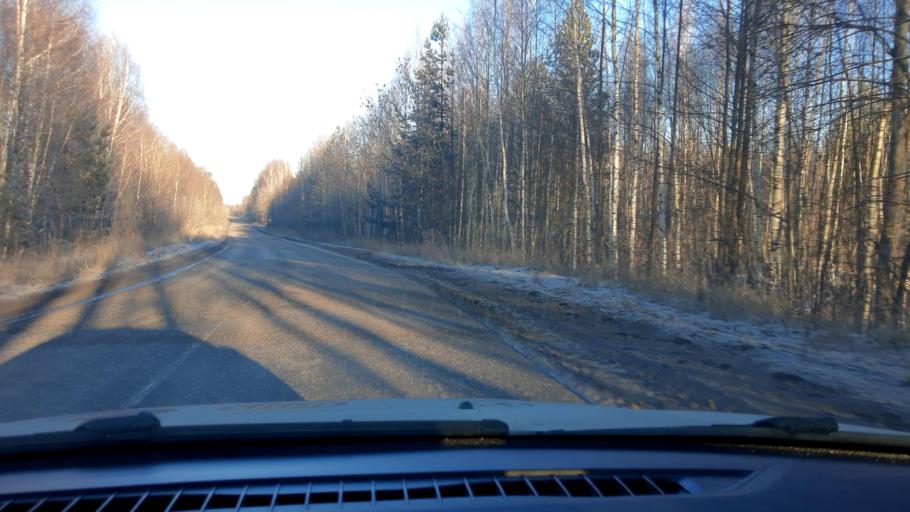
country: RU
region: Nizjnij Novgorod
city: Novosmolinskiy
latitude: 56.2938
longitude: 43.0274
